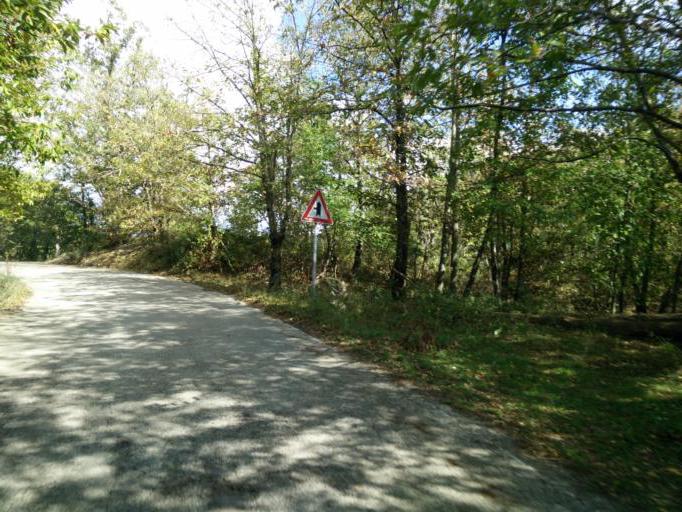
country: IT
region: Liguria
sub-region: Provincia di La Spezia
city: Sesta Godano
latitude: 44.3417
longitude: 9.7018
